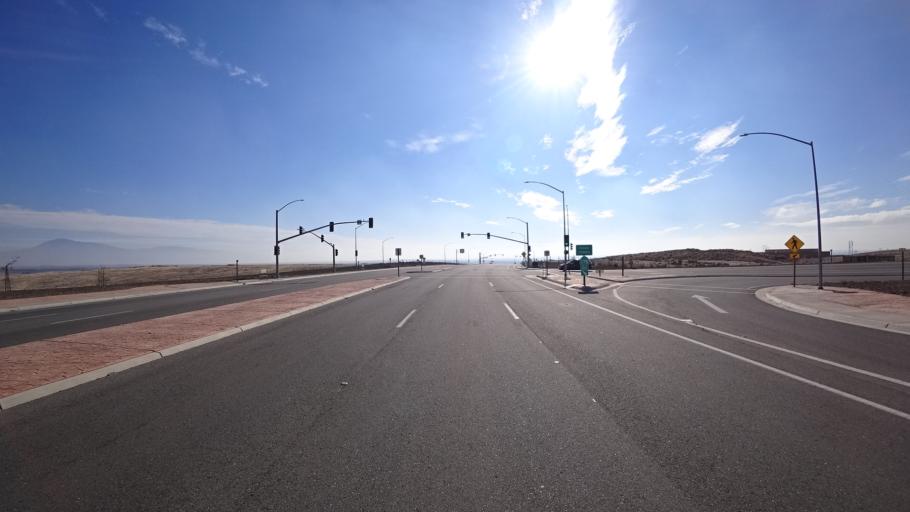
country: US
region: California
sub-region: Kern County
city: Bakersfield
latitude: 35.3960
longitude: -118.9132
